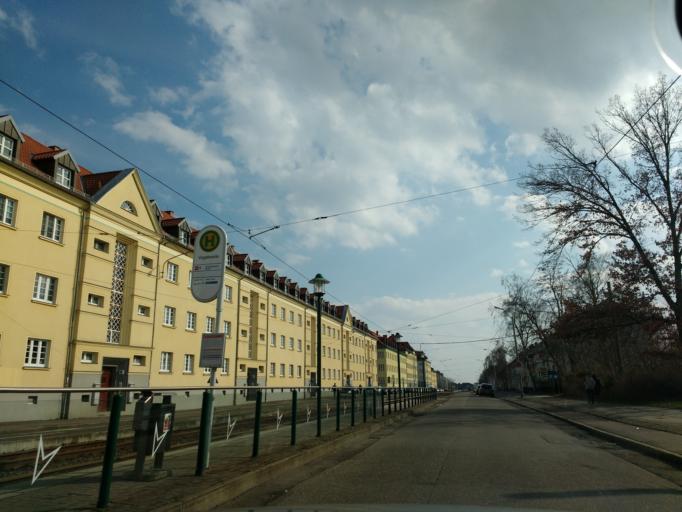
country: DE
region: Saxony-Anhalt
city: Halle (Saale)
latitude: 51.4564
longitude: 11.9724
